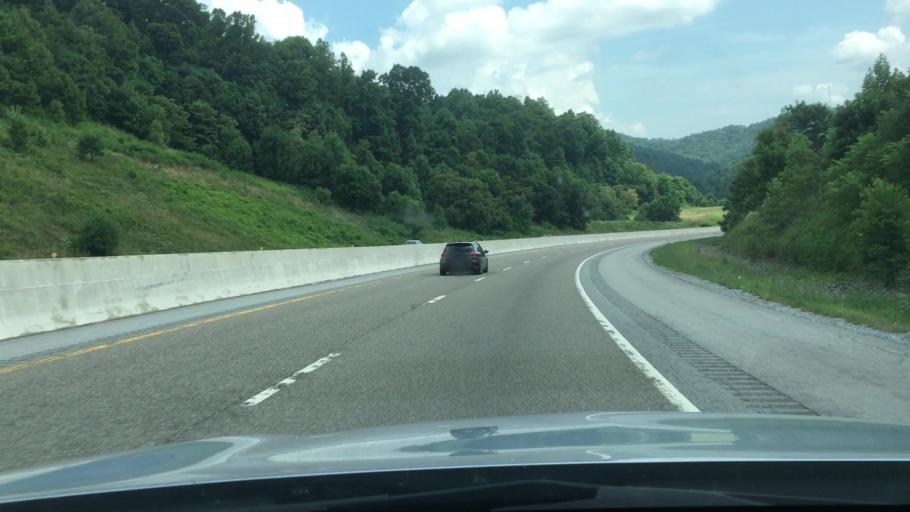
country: US
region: North Carolina
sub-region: Madison County
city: Mars Hill
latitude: 35.9964
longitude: -82.5438
